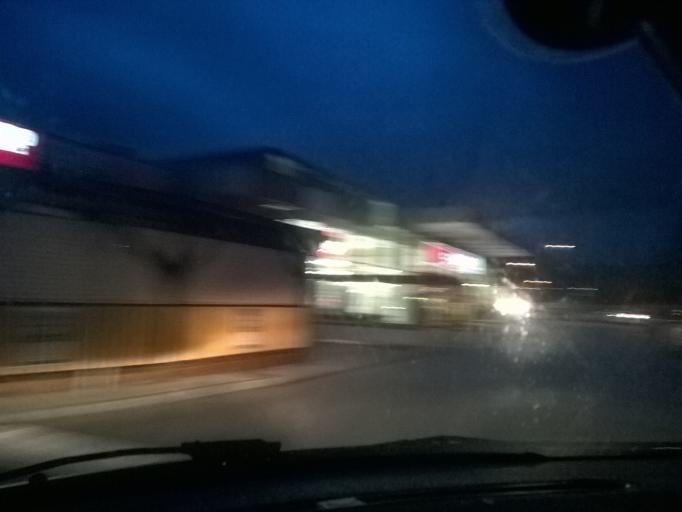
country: SI
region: Rogaska Slatina
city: Rogaska Slatina
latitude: 46.2245
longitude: 15.6423
